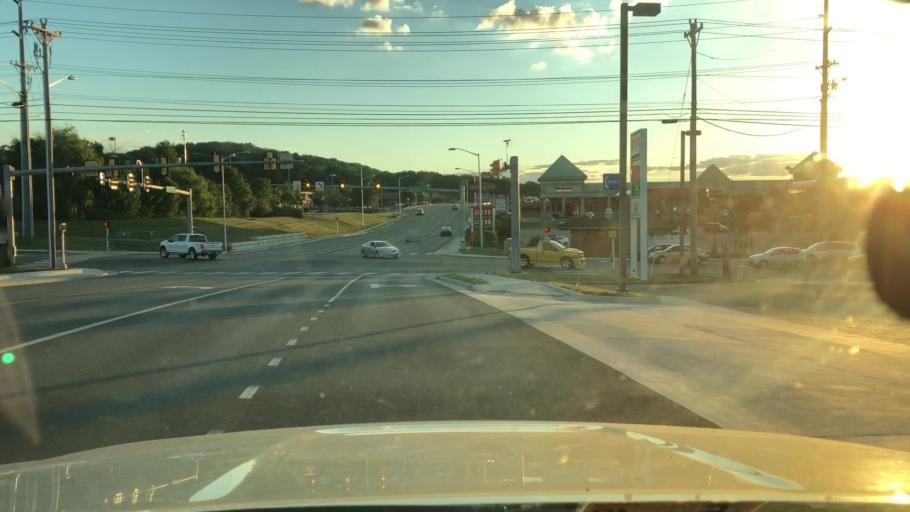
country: US
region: Virginia
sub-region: City of Harrisonburg
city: Harrisonburg
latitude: 38.4291
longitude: -78.8548
